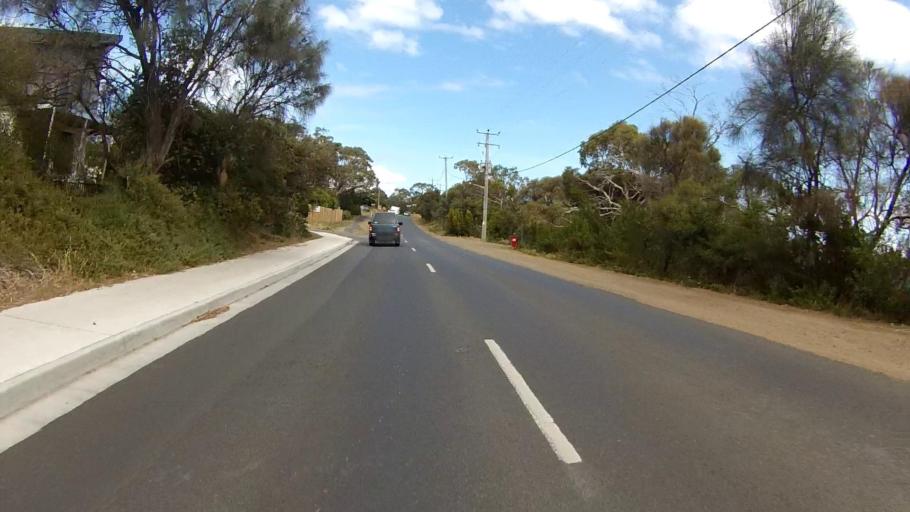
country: AU
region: Tasmania
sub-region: Sorell
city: Sorell
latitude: -42.8626
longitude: 147.6118
